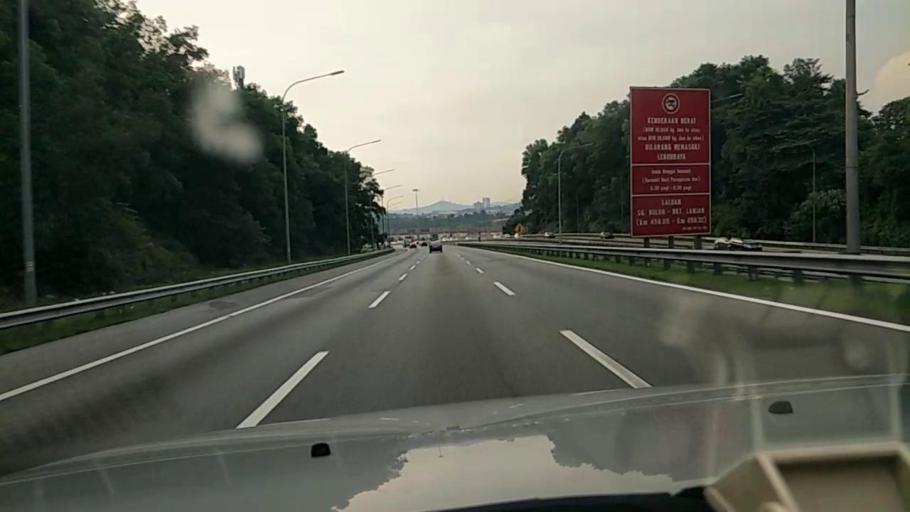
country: MY
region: Selangor
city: Kampung Baru Subang
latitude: 3.1808
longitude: 101.5984
